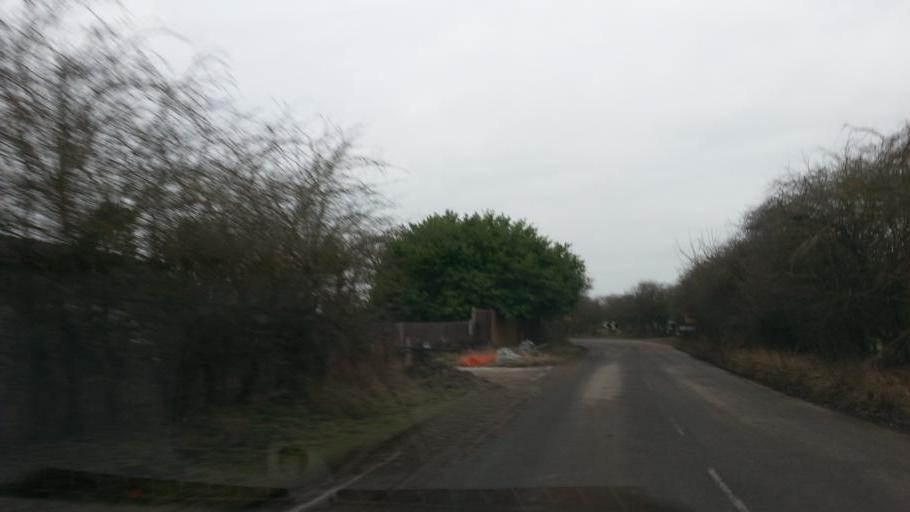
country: GB
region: England
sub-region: Central Bedfordshire
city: Totternhoe
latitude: 51.9100
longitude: -0.5731
